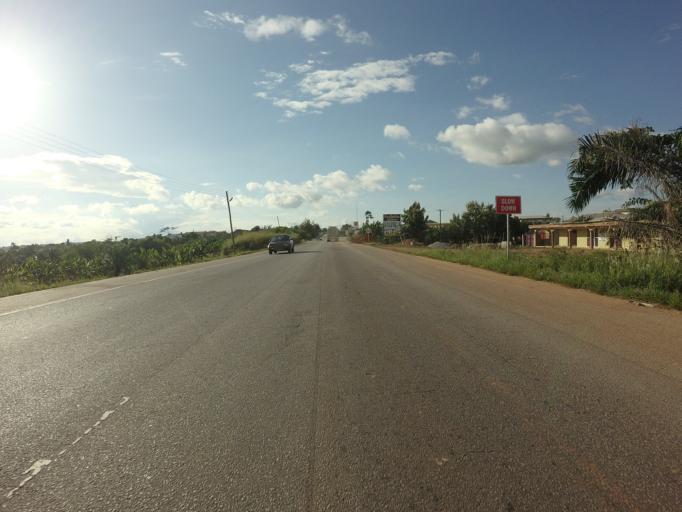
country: GH
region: Ashanti
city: Tafo
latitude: 6.9135
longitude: -1.6581
